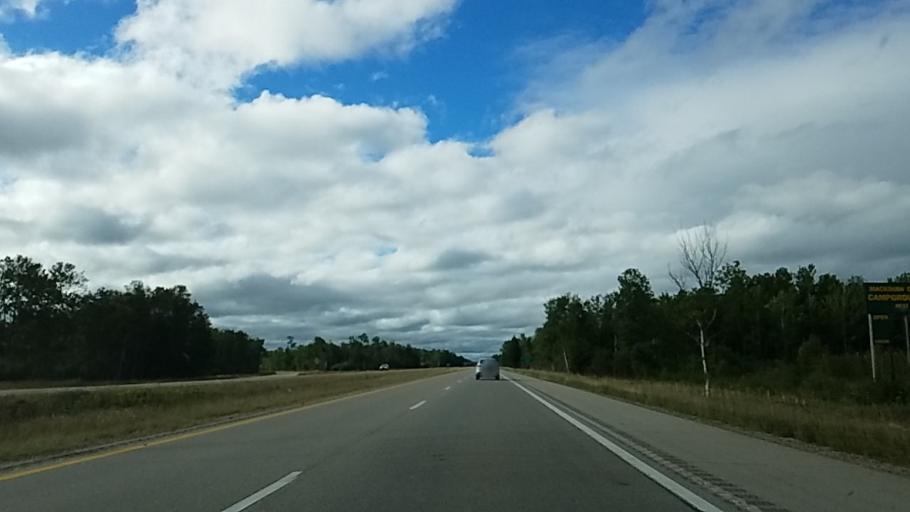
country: US
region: Michigan
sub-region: Mackinac County
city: Saint Ignace
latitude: 45.7445
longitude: -84.7289
